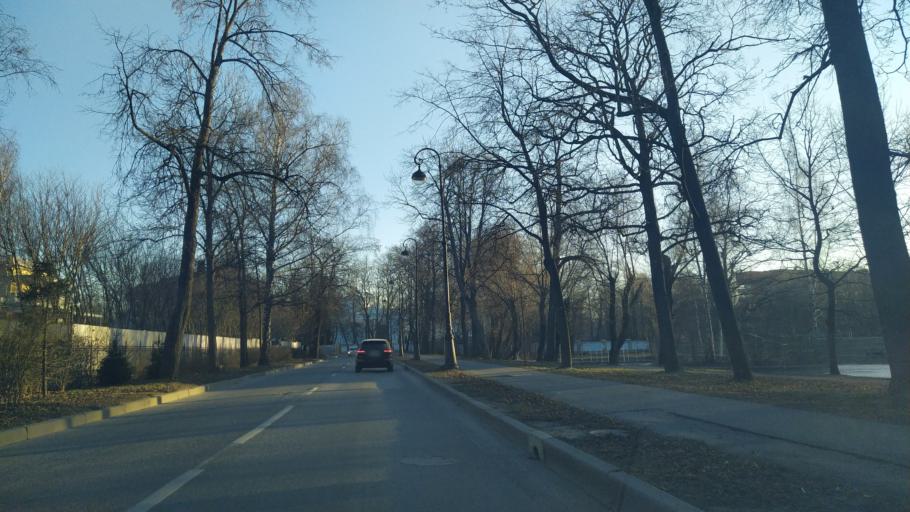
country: RU
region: St.-Petersburg
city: Novaya Derevnya
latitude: 59.9755
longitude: 30.2791
